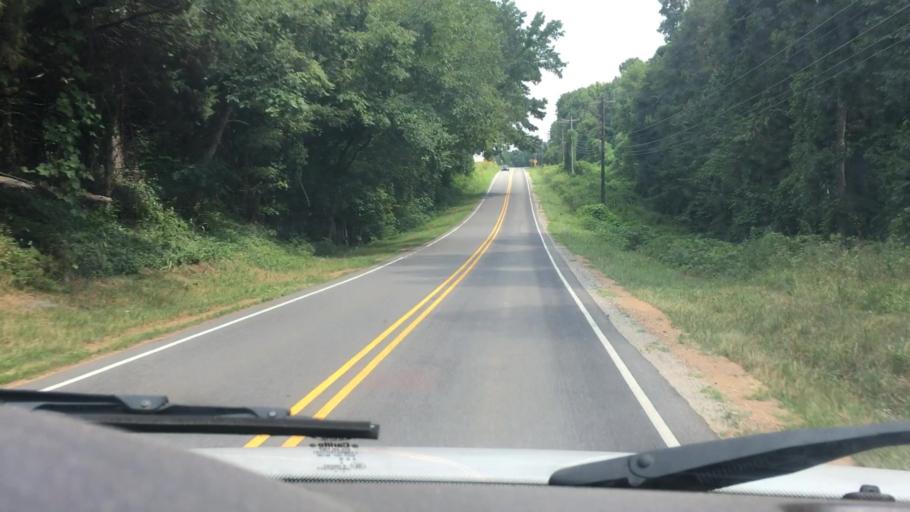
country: US
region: North Carolina
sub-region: Gaston County
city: Davidson
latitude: 35.4586
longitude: -80.8053
